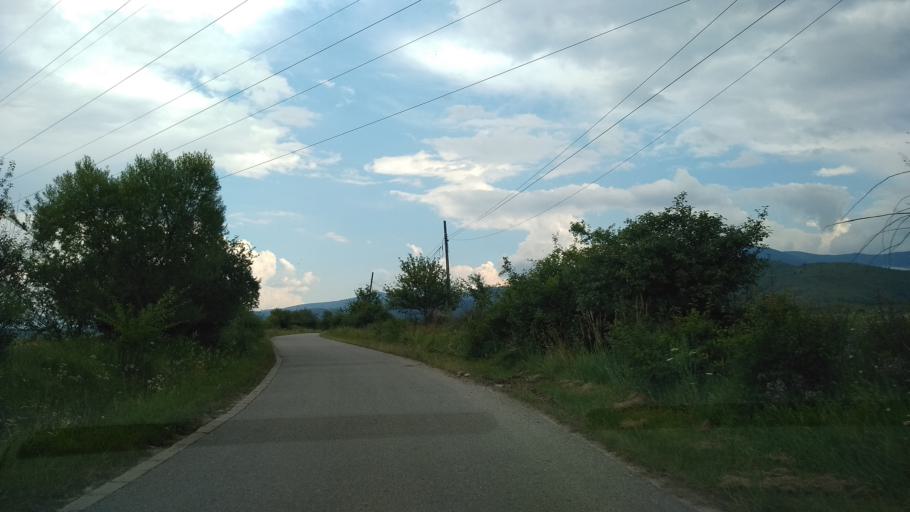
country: RO
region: Hunedoara
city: Salasu de Sus
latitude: 45.5026
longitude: 22.9644
